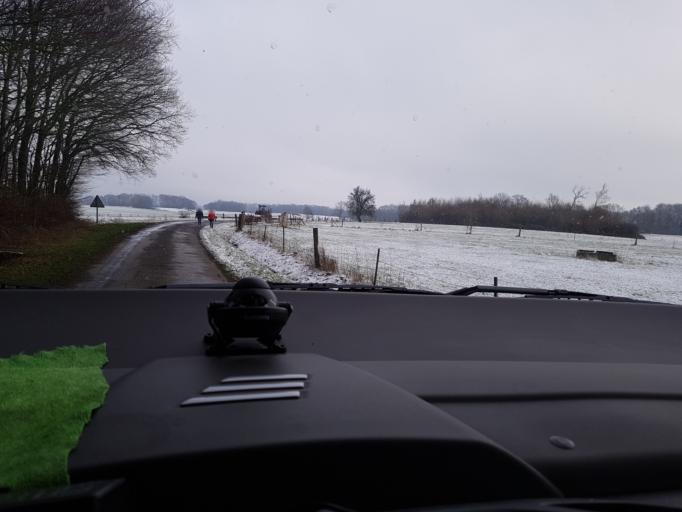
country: FR
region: Champagne-Ardenne
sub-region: Departement des Ardennes
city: Signy-le-Petit
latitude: 49.8369
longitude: 4.3834
